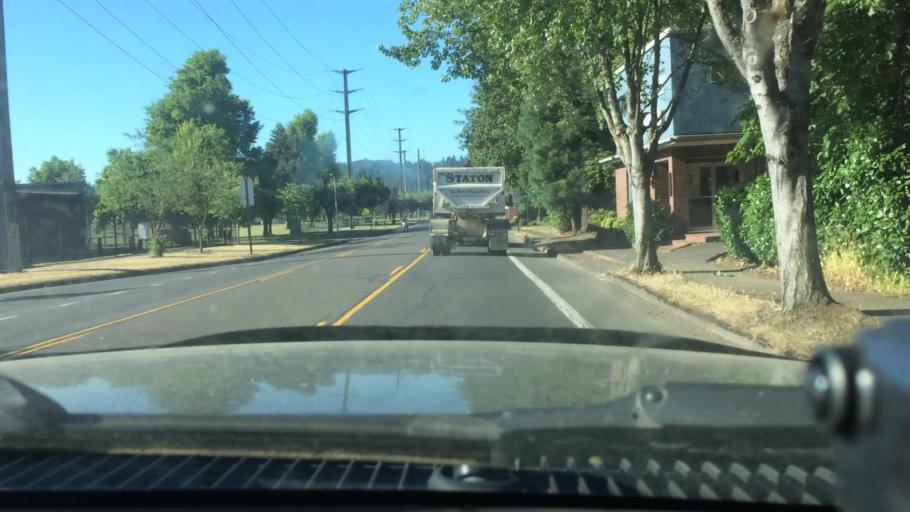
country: US
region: Oregon
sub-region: Lane County
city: Eugene
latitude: 44.0452
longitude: -123.1182
